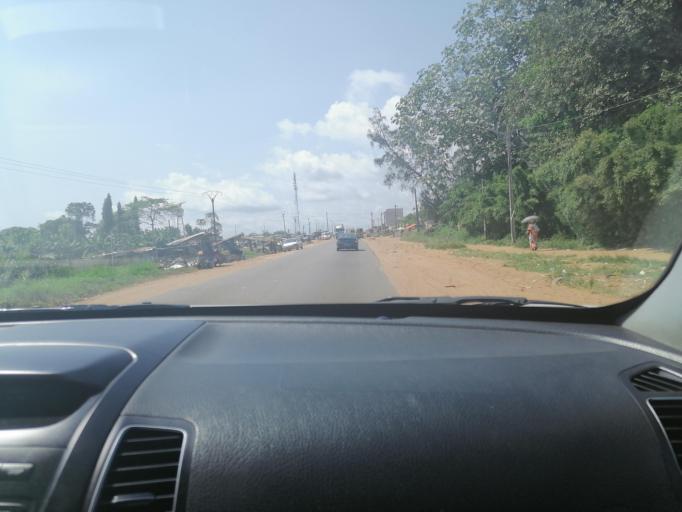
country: CI
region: Lagunes
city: Songon
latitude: 5.3378
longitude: -4.1388
